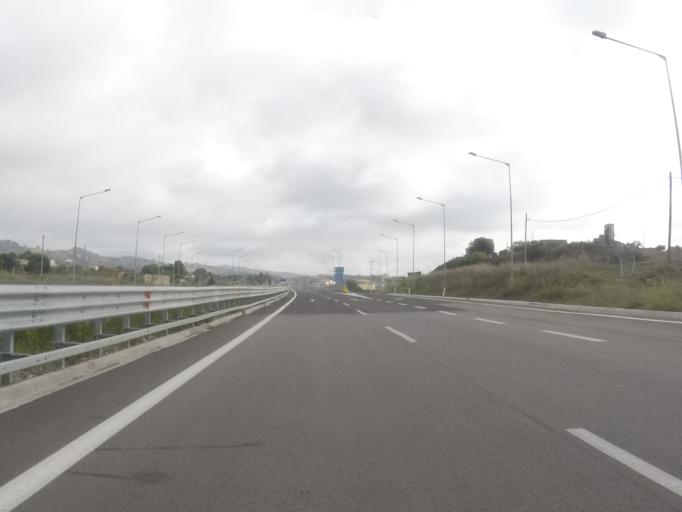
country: IT
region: Sicily
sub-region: Agrigento
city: Grotte
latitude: 37.3727
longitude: 13.7149
